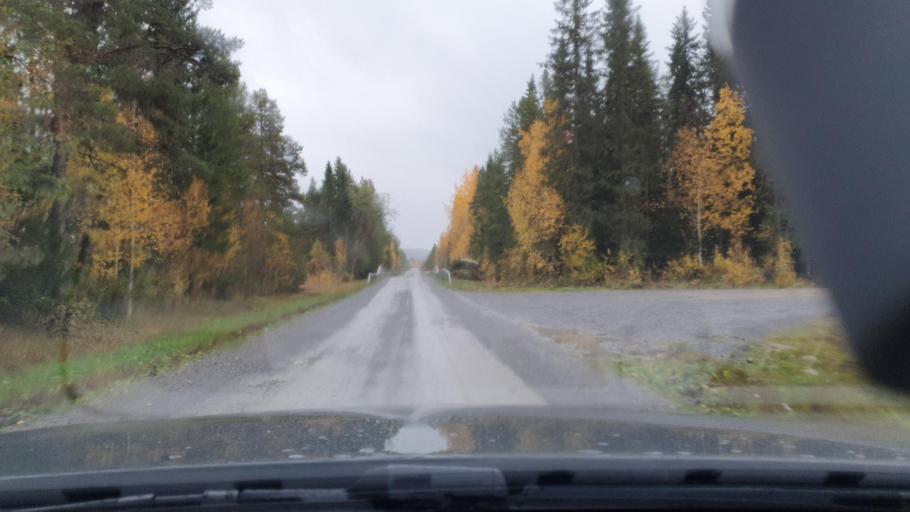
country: SE
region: Jaemtland
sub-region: Stroemsunds Kommun
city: Stroemsund
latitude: 63.5430
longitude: 15.5689
